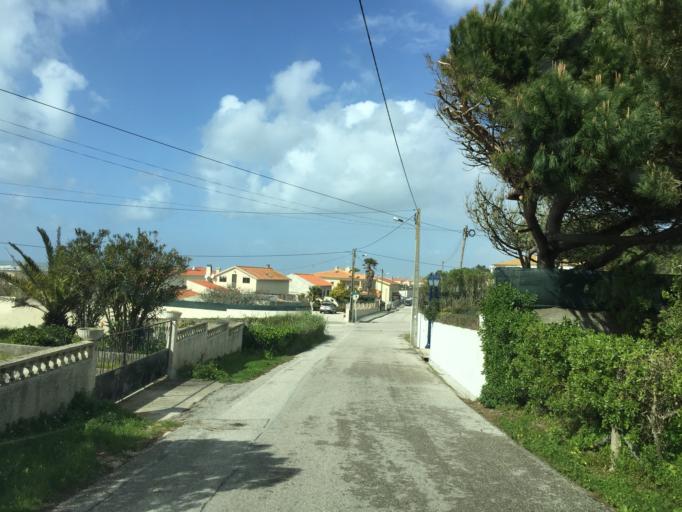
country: PT
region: Coimbra
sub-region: Figueira da Foz
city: Buarcos
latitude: 40.2082
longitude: -8.8949
